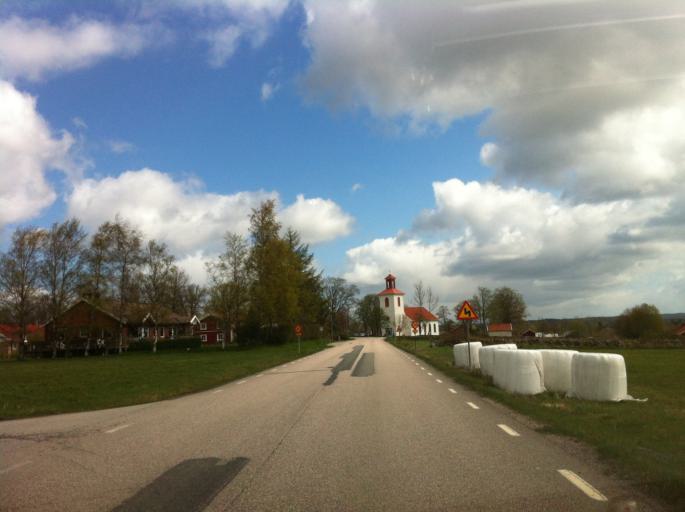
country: SE
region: Vaestra Goetaland
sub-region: Alingsas Kommun
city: Ingared
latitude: 57.8149
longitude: 12.5568
